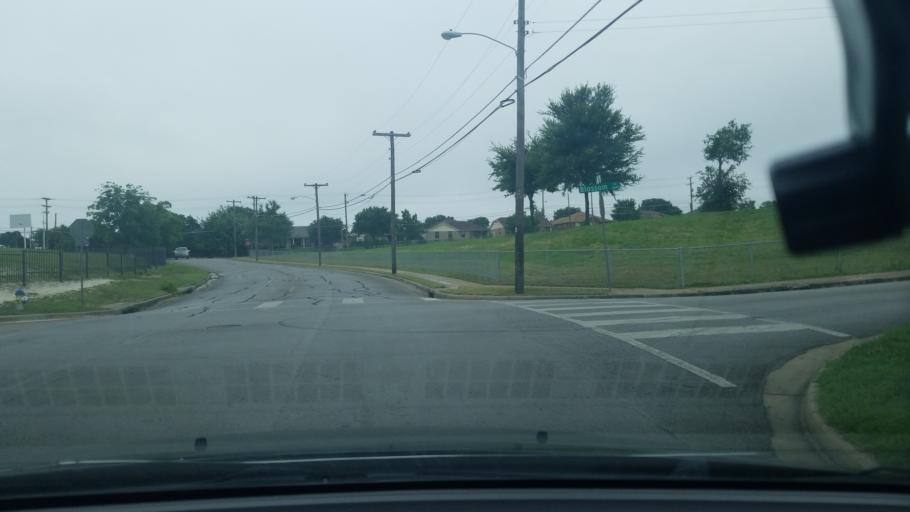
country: US
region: Texas
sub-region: Dallas County
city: Balch Springs
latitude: 32.7594
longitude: -96.6876
